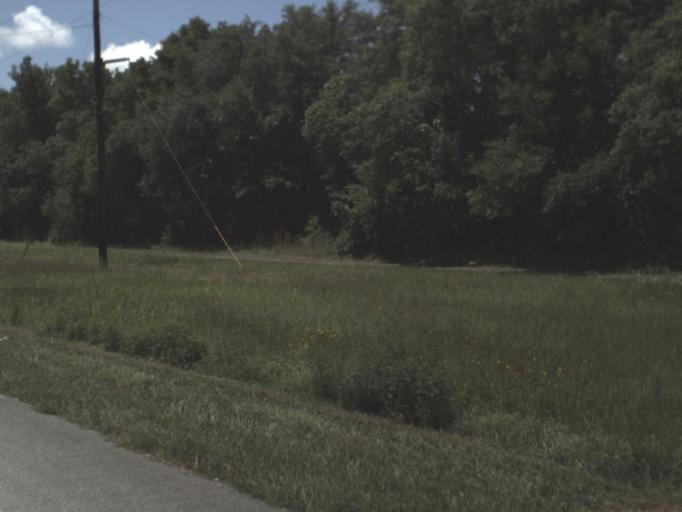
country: US
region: Florida
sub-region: Putnam County
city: Crescent City
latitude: 29.5055
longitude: -81.6045
